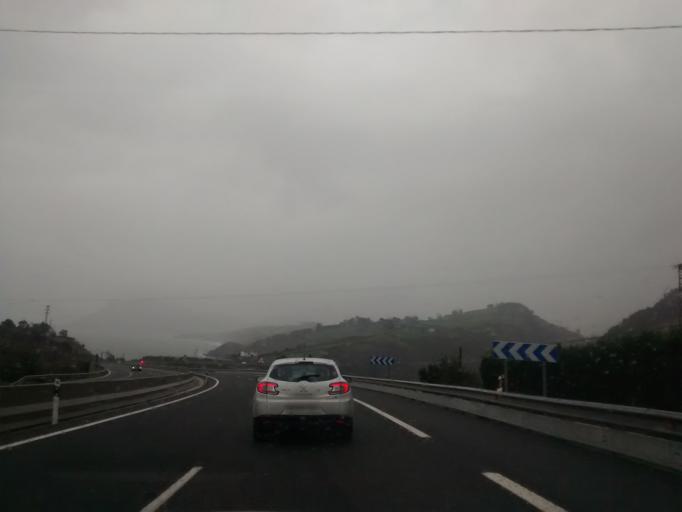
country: ES
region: Cantabria
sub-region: Provincia de Cantabria
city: Castro-Urdiales
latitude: 43.3535
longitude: -3.1785
